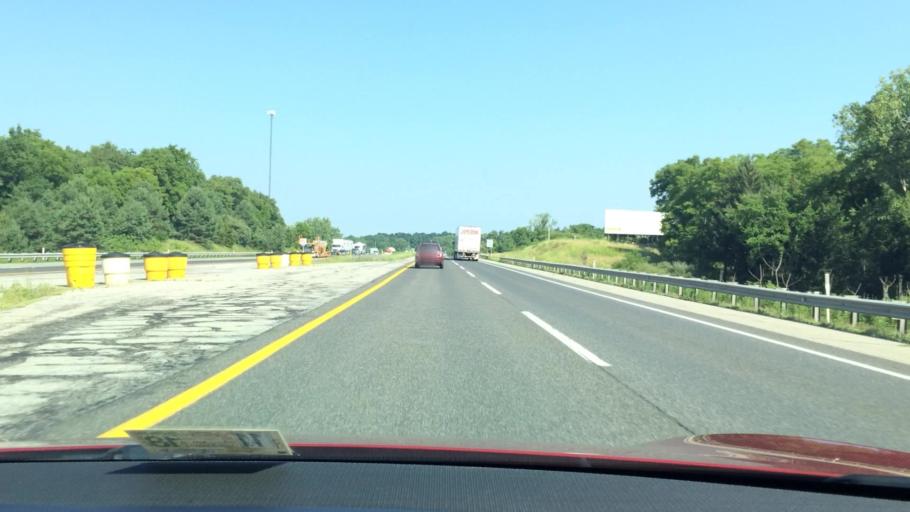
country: US
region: Indiana
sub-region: Steuben County
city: Fremont
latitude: 41.7425
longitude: -85.0173
